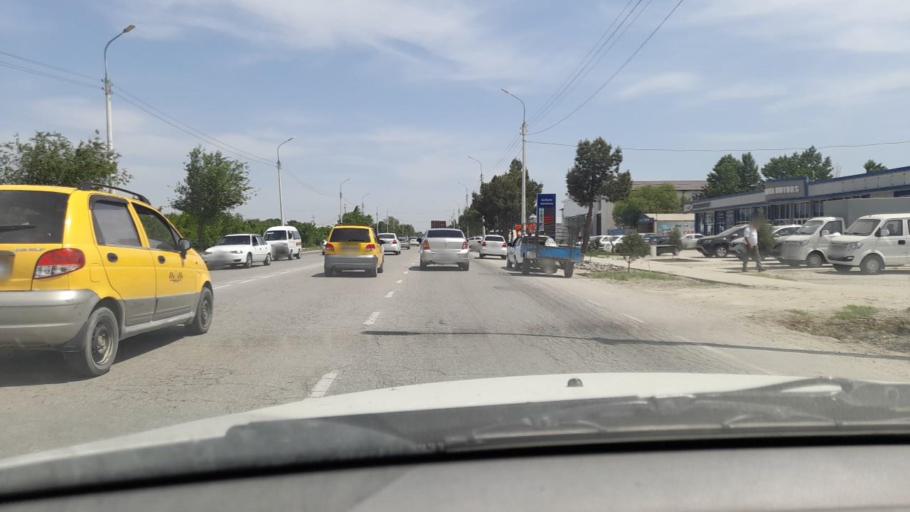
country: UZ
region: Navoiy
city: Karmana Shahri
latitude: 40.1472
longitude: 65.3313
